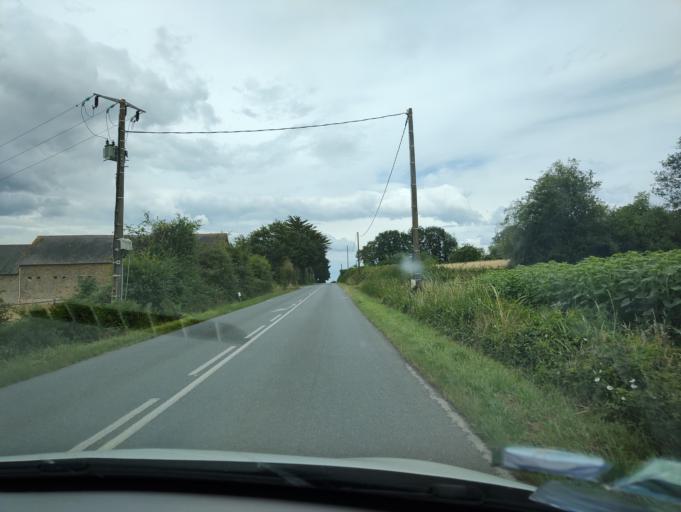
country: FR
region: Pays de la Loire
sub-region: Departement de la Loire-Atlantique
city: Chateaubriant
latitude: 47.7113
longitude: -1.4055
